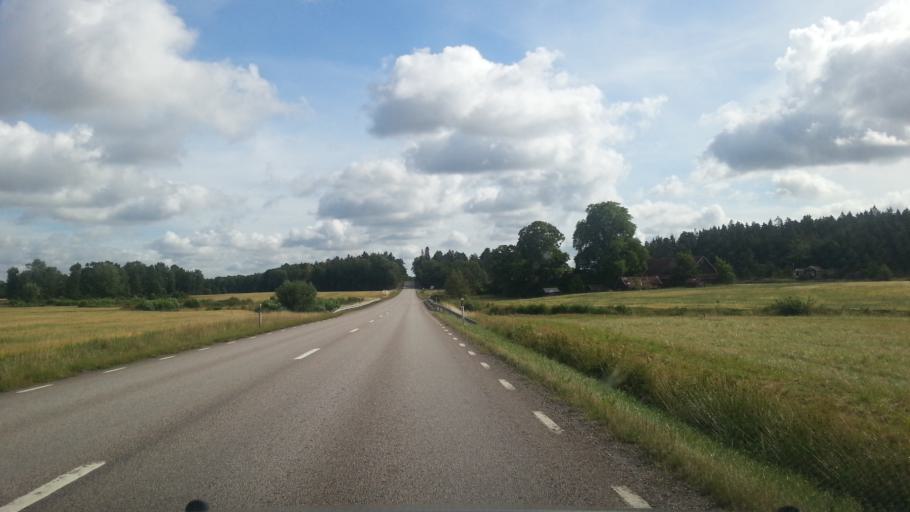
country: SE
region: Vaestra Goetaland
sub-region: Vara Kommun
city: Vara
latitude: 58.4234
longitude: 12.8769
